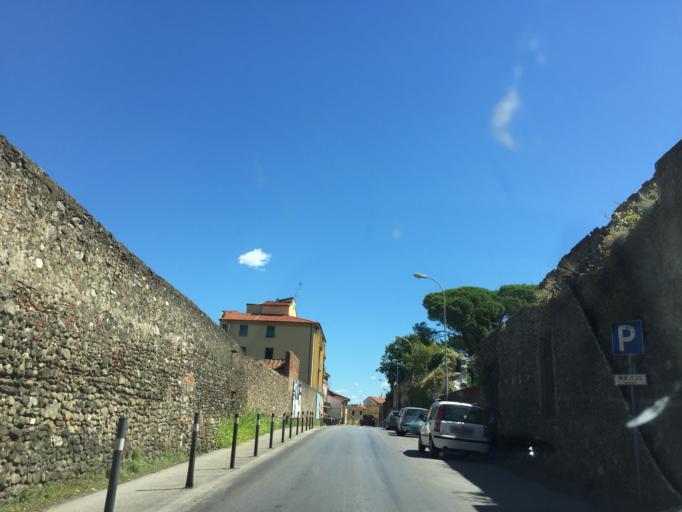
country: IT
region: Tuscany
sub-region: Provincia di Pistoia
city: Pistoia
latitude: 43.9293
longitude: 10.9157
